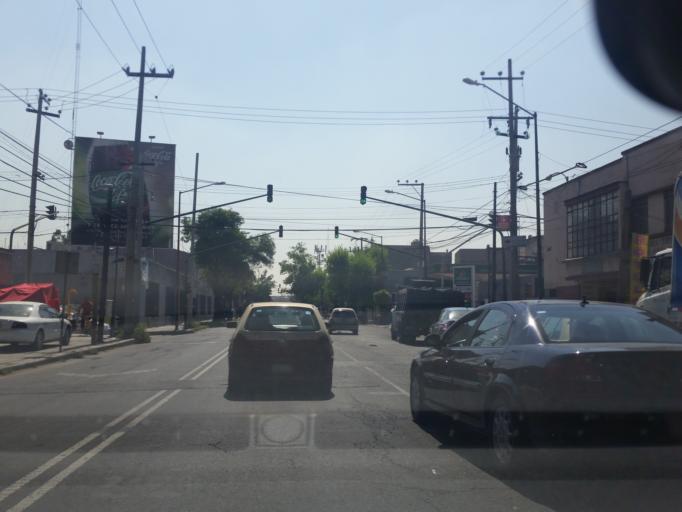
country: MX
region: Mexico City
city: Cuauhtemoc
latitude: 19.4554
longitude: -99.1615
